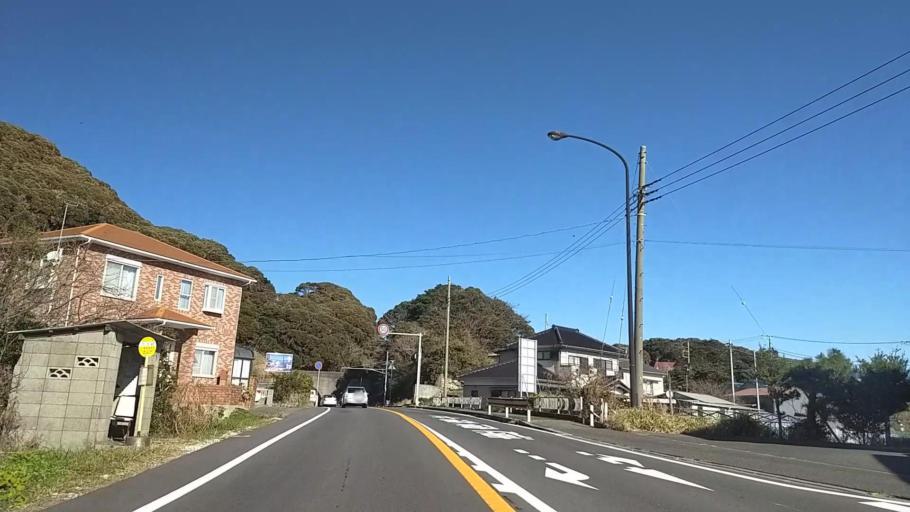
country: JP
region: Chiba
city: Kawaguchi
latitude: 35.0650
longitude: 140.0771
